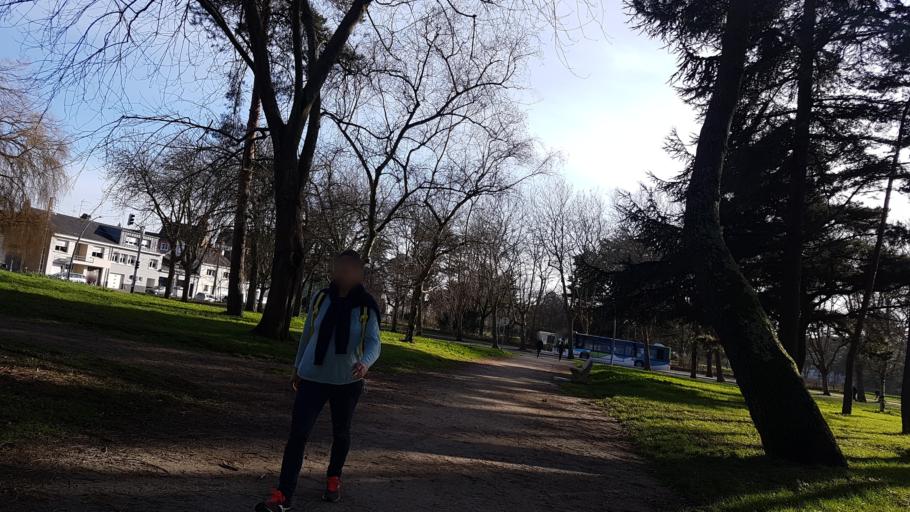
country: FR
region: Pays de la Loire
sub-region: Departement de la Loire-Atlantique
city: Saint-Nazaire
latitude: 47.2719
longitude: -2.2227
